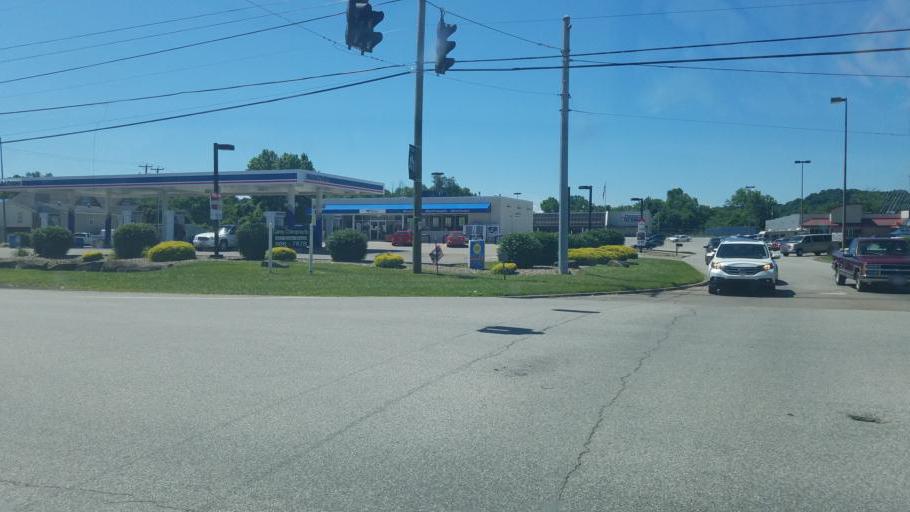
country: US
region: West Virginia
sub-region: Cabell County
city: Huntington
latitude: 38.4391
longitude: -82.3868
